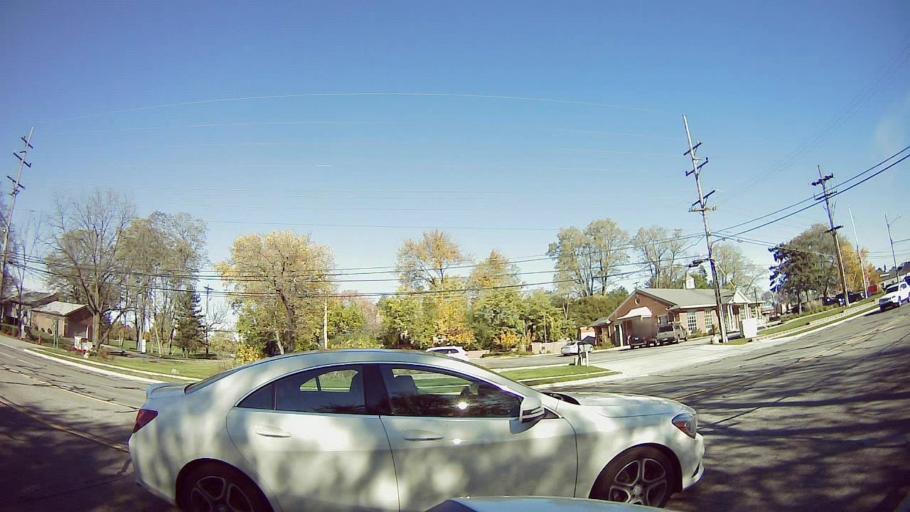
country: US
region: Michigan
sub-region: Oakland County
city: Bingham Farms
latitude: 42.5452
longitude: -83.2648
